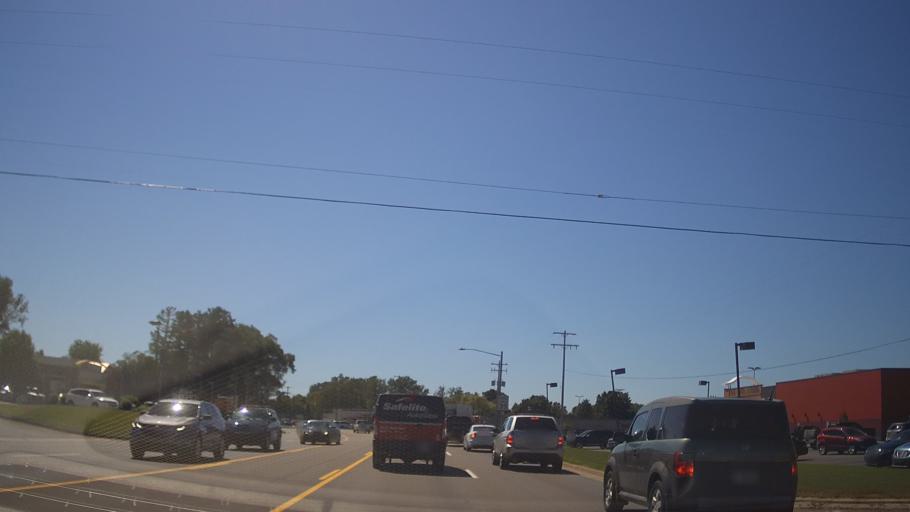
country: US
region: Michigan
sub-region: Emmet County
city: Petoskey
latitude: 45.3895
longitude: -84.9163
